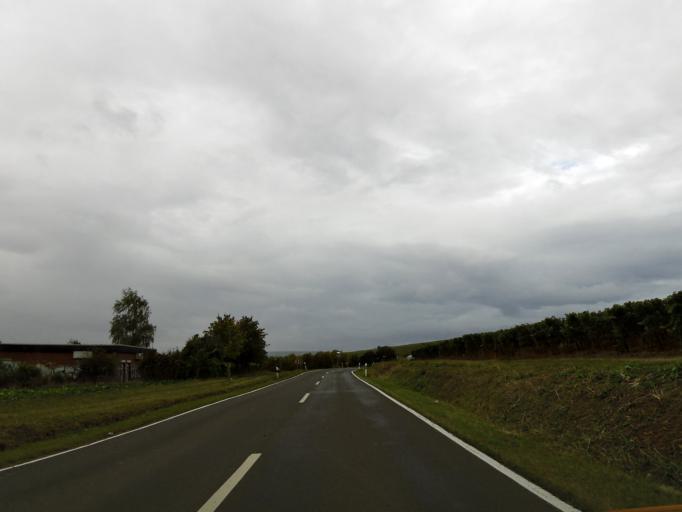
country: DE
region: Rheinland-Pfalz
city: Siefersheim
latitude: 49.8135
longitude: 7.9504
